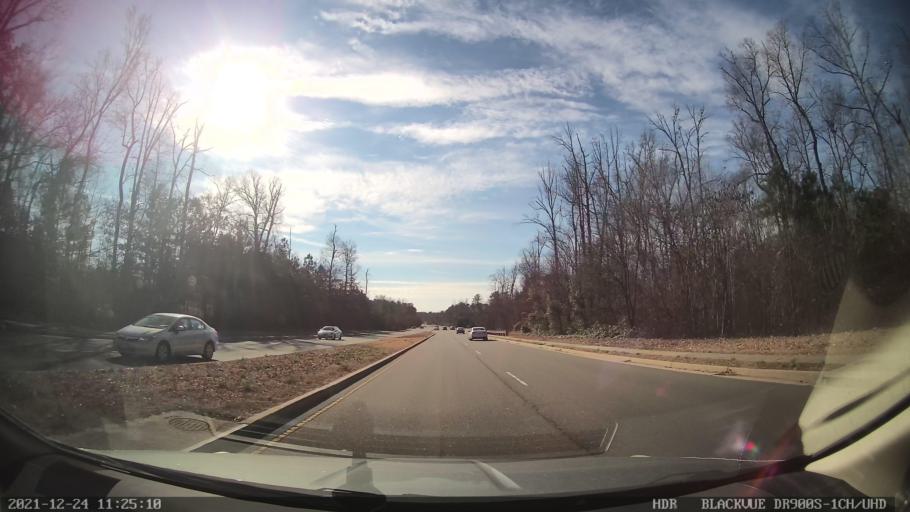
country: US
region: Virginia
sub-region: Henrico County
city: Short Pump
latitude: 37.6470
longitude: -77.6094
